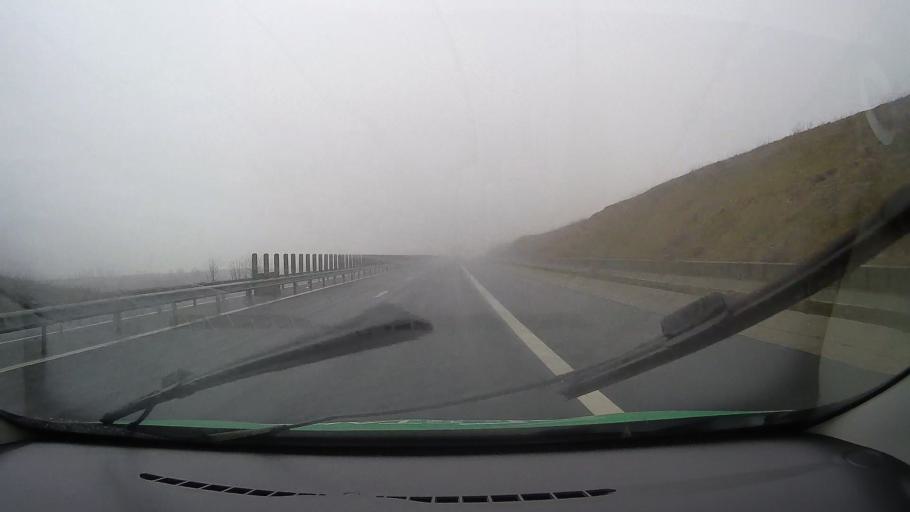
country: RO
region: Timis
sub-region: Comuna Manastiur
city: Manastiur
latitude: 45.8154
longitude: 22.0538
